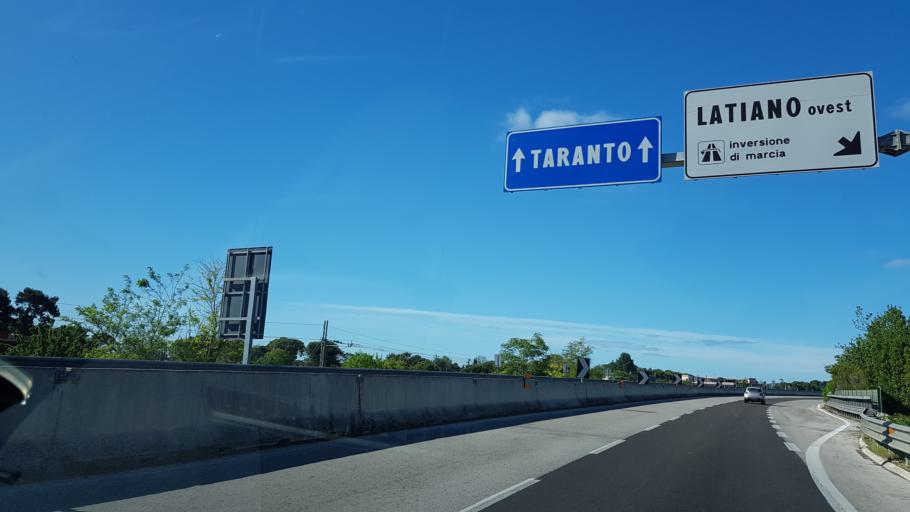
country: IT
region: Apulia
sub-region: Provincia di Brindisi
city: Latiano
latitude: 40.5513
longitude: 17.7075
